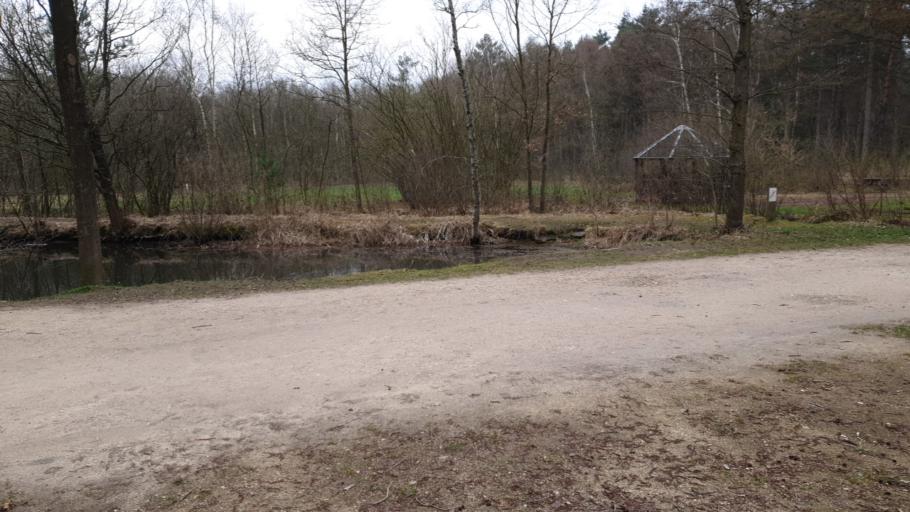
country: BE
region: Flanders
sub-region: Provincie Antwerpen
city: Brasschaat
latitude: 51.3116
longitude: 4.5242
